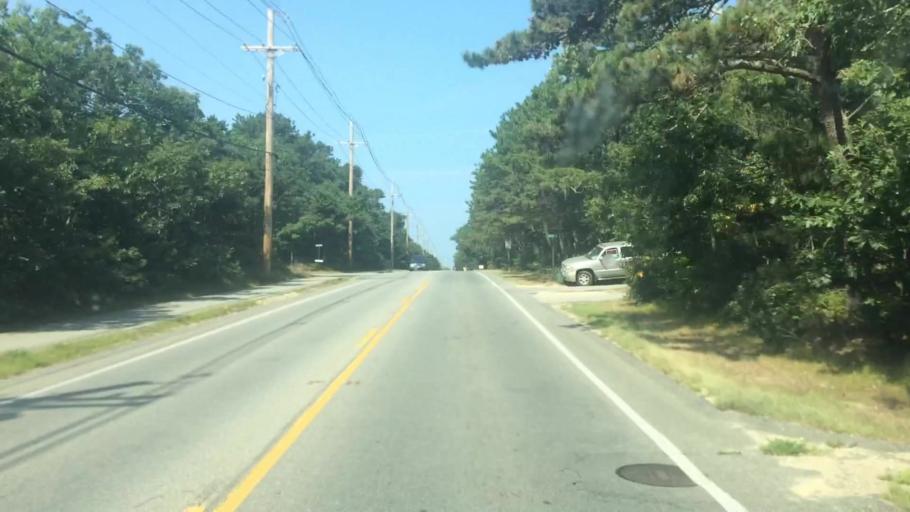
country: US
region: Massachusetts
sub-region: Dukes County
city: Vineyard Haven
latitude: 41.4171
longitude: -70.5879
